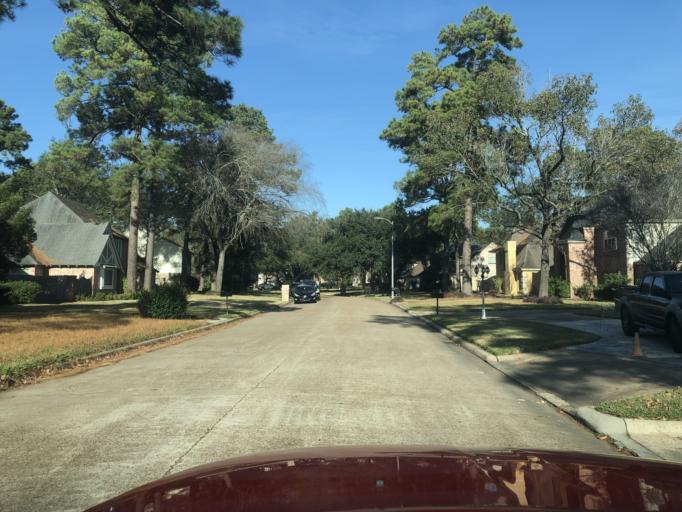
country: US
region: Texas
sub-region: Harris County
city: Spring
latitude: 30.0156
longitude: -95.4634
